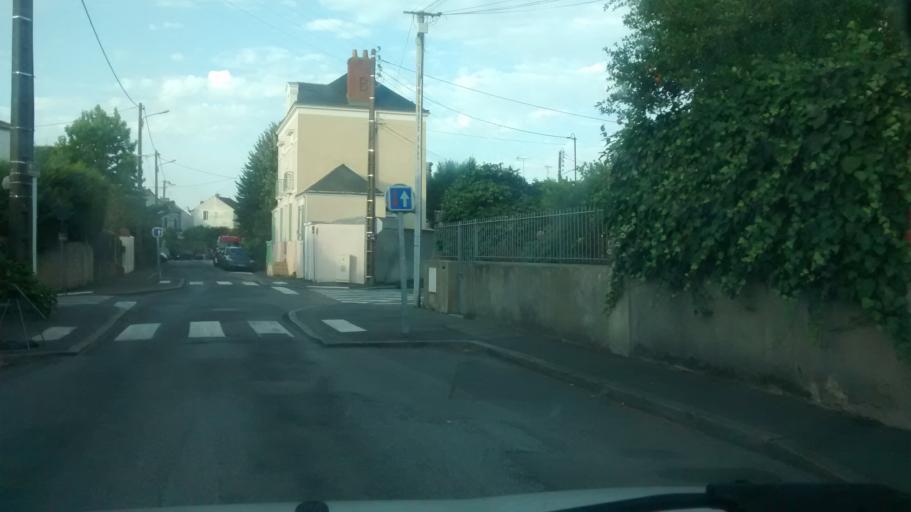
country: FR
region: Pays de la Loire
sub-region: Departement de la Loire-Atlantique
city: Reze
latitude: 47.1926
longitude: -1.5837
